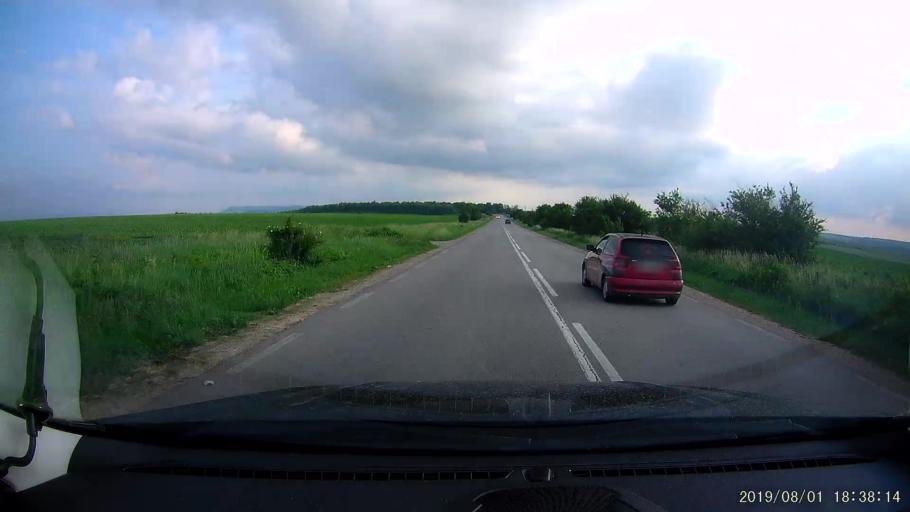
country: BG
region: Shumen
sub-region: Obshtina Khitrino
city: Gara Khitrino
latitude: 43.4053
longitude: 26.9192
